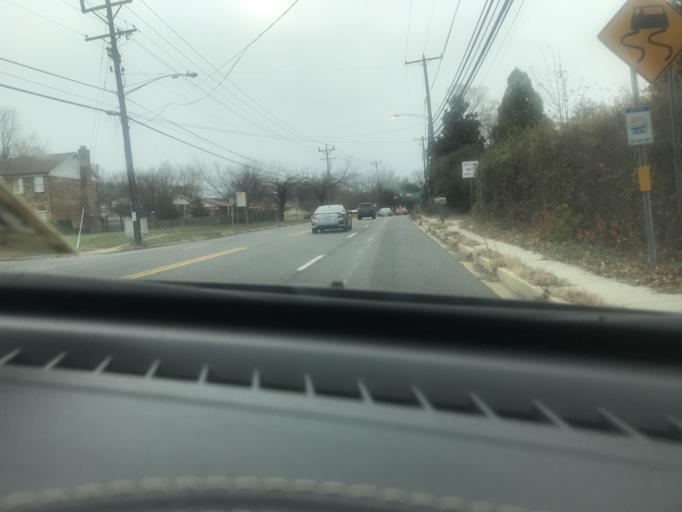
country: US
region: Maryland
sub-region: Prince George's County
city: Temple Hills
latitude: 38.7777
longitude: -76.9507
